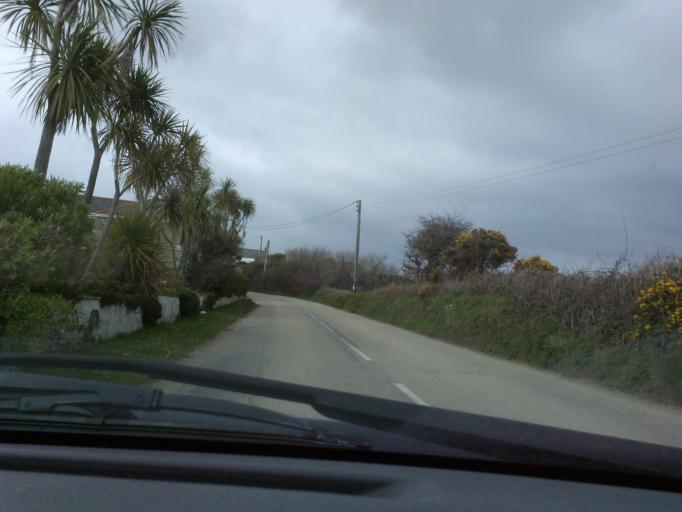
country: GB
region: England
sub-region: Cornwall
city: Sennen
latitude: 50.0568
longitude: -5.6665
